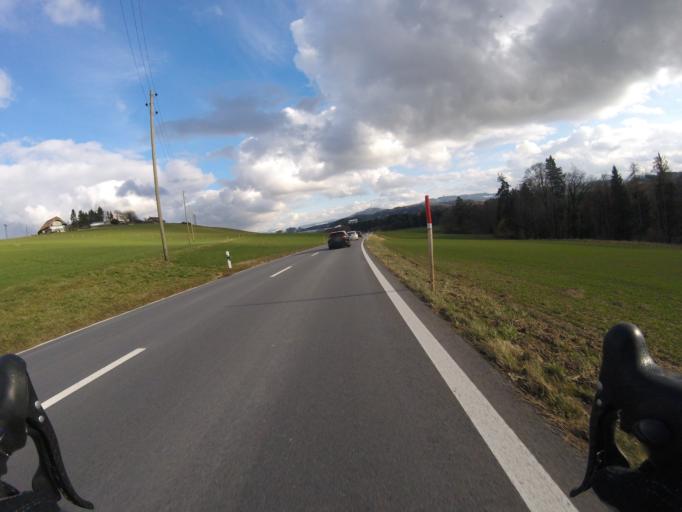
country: CH
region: Bern
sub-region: Bern-Mittelland District
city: Frauenkappelen
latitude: 46.9496
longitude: 7.3570
